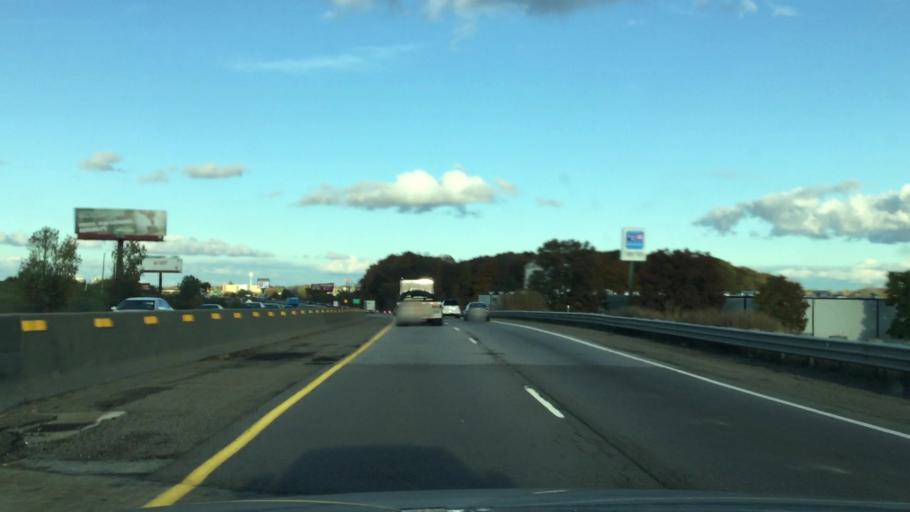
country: US
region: Michigan
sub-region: Kalamazoo County
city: Eastwood
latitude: 42.2503
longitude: -85.5451
